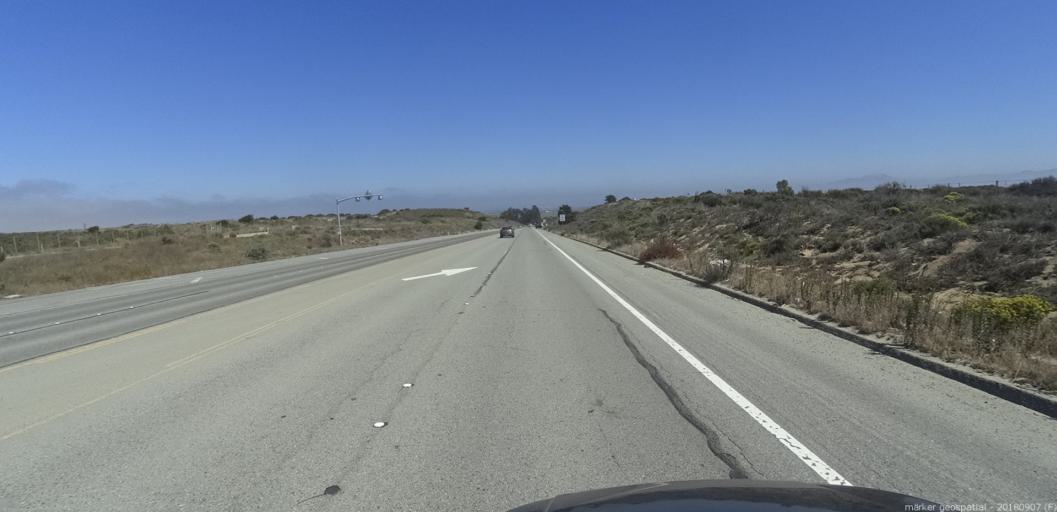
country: US
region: California
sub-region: Monterey County
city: Marina
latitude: 36.6712
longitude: -121.7535
